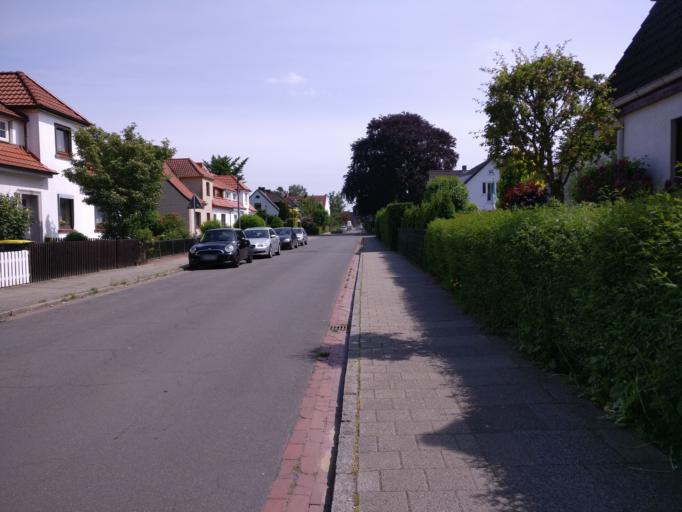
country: DE
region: Lower Saxony
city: Lilienthal
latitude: 53.1049
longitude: 8.8733
